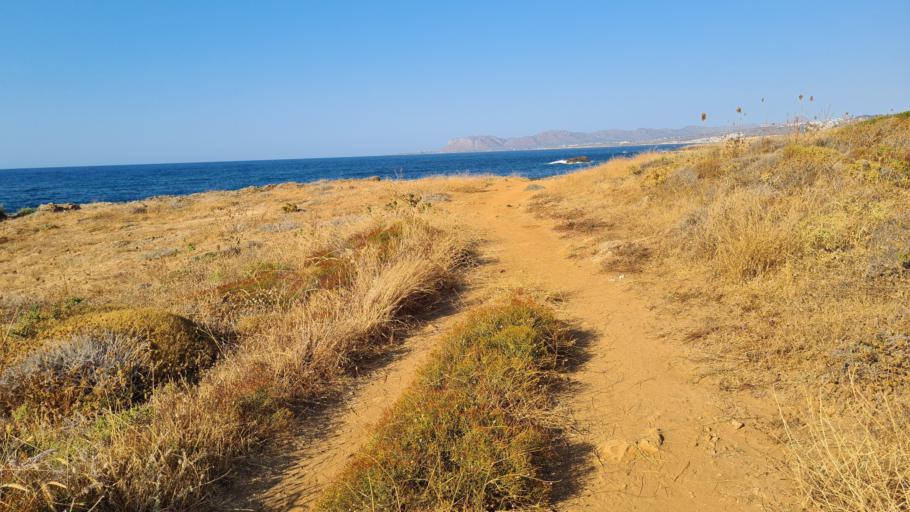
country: GR
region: Crete
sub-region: Nomos Chanias
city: Daratsos
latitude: 35.5161
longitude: 23.9813
